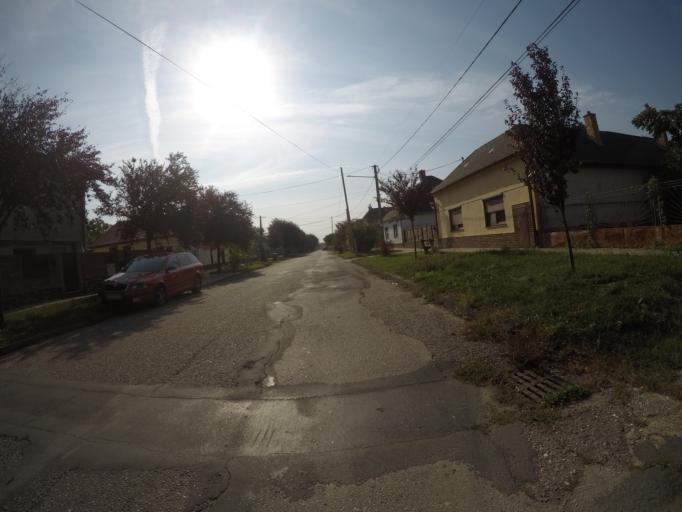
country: SK
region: Trnavsky
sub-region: Okres Dunajska Streda
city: Velky Meder
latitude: 47.8534
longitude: 17.7645
